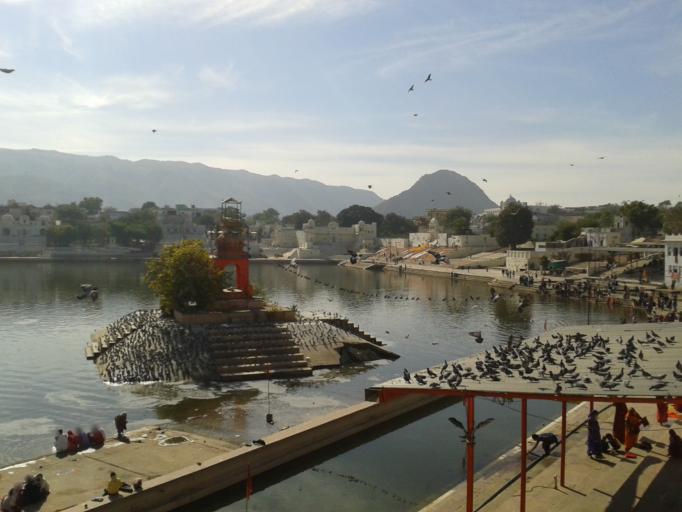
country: IN
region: Rajasthan
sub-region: Ajmer
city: Pushkar
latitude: 26.4883
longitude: 74.5527
